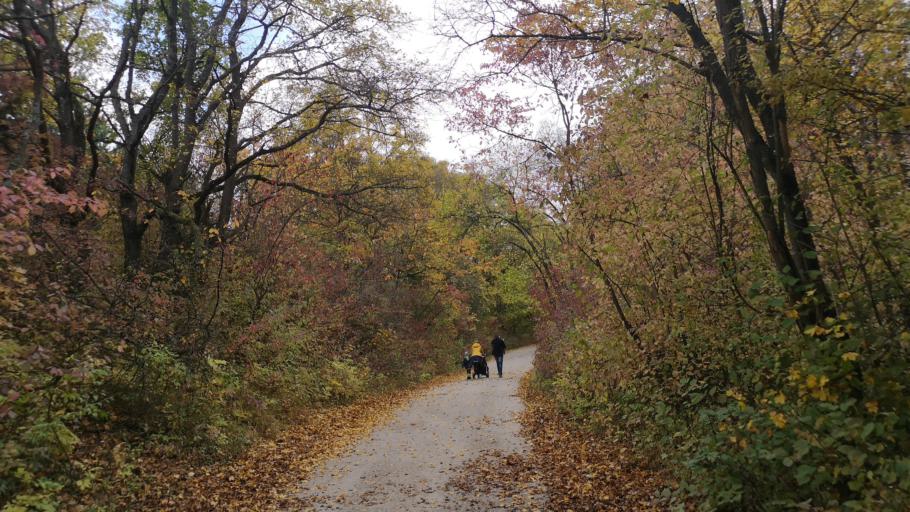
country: SK
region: Nitriansky
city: Cachtice
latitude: 48.7186
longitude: 17.7657
